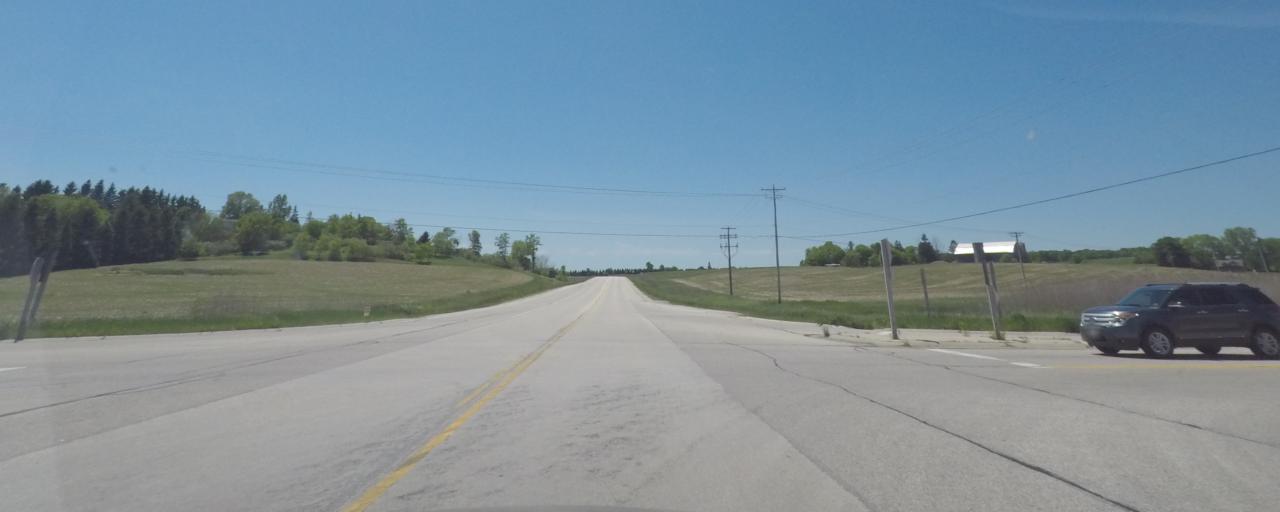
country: US
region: Wisconsin
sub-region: Washington County
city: West Bend
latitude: 43.4987
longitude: -88.1355
